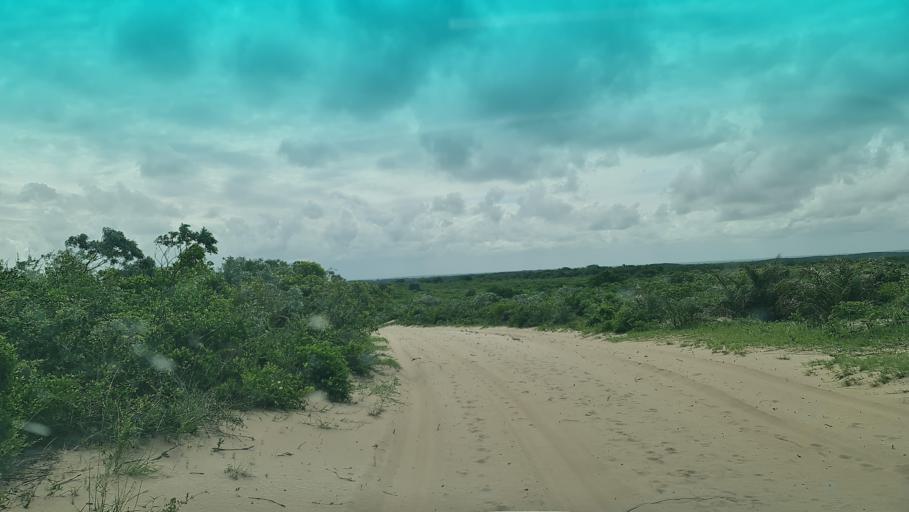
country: MZ
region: Maputo
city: Manhica
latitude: -25.4416
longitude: 32.9430
